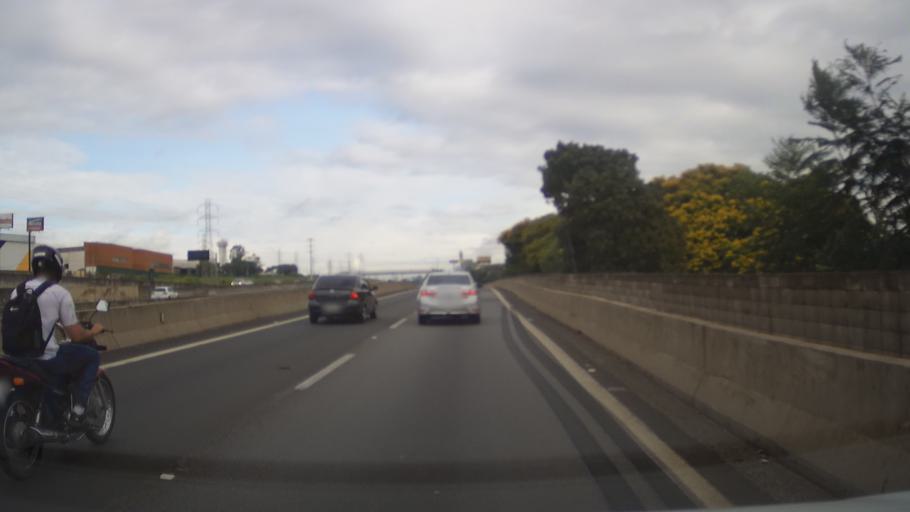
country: BR
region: Sao Paulo
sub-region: Campinas
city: Campinas
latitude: -22.9267
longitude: -47.0844
